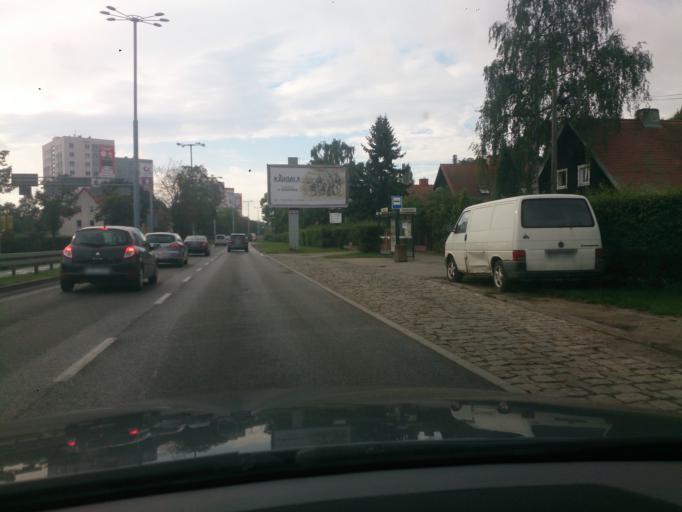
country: PL
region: Pomeranian Voivodeship
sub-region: Sopot
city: Sopot
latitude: 54.4230
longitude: 18.5640
